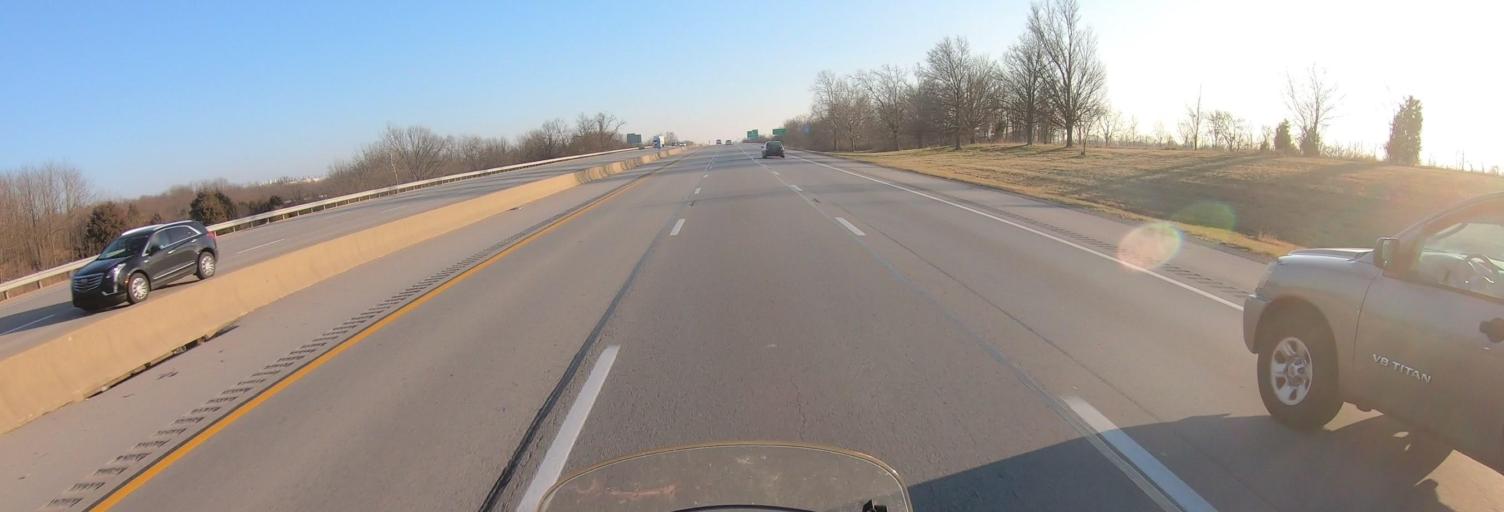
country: US
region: Kentucky
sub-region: Scott County
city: Georgetown
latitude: 38.2687
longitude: -84.5555
